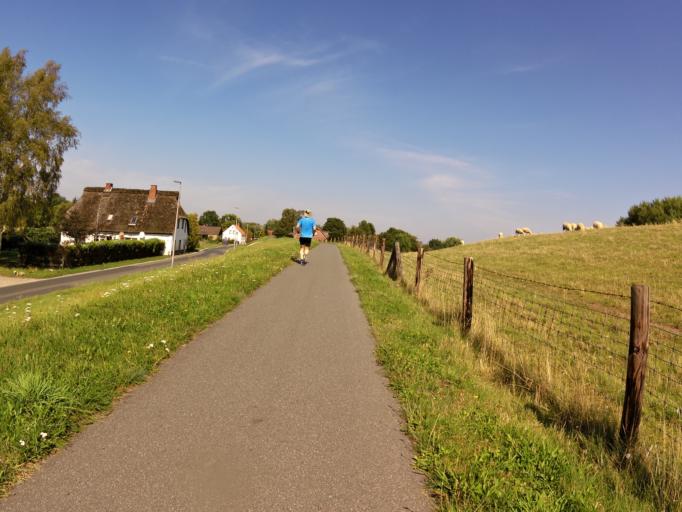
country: DE
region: Lower Saxony
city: Brake (Unterweser)
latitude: 53.2869
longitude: 8.4815
